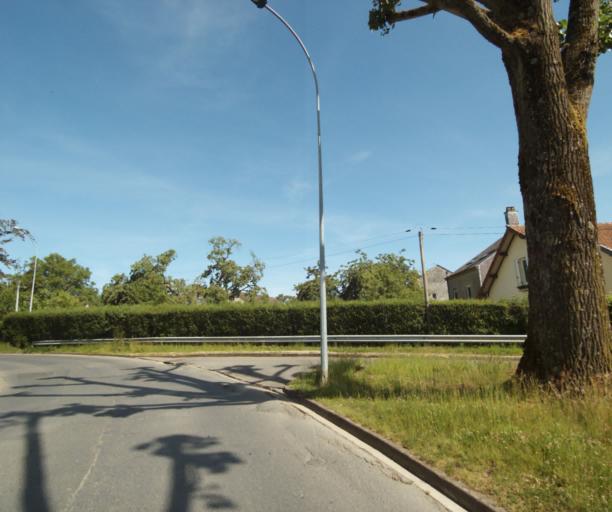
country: FR
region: Champagne-Ardenne
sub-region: Departement des Ardennes
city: La Francheville
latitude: 49.7461
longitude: 4.7251
